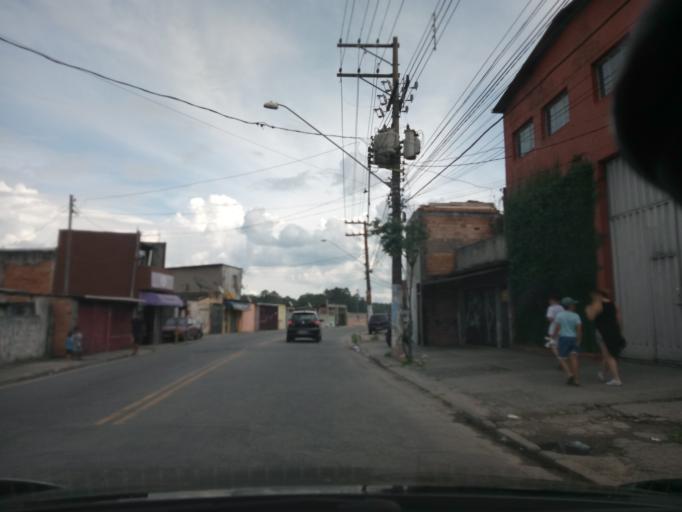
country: BR
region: Sao Paulo
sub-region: Diadema
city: Diadema
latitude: -23.7430
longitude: -46.6037
